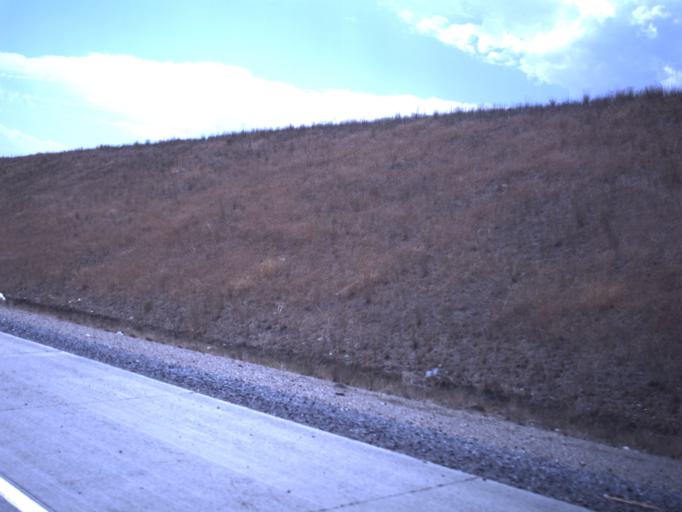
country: US
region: Utah
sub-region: Salt Lake County
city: Oquirrh
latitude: 40.6169
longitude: -112.0412
